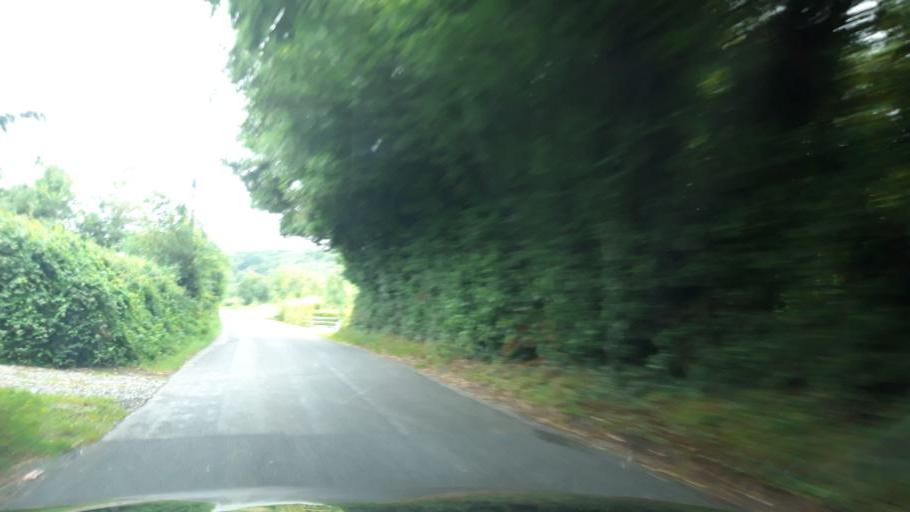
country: IE
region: Leinster
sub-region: Kilkenny
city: Ballyragget
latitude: 52.7218
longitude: -7.4022
